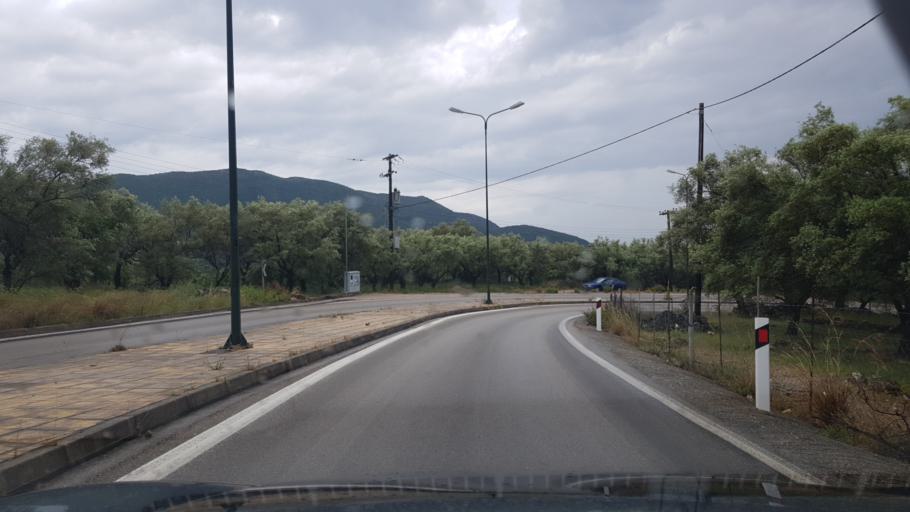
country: GR
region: Ionian Islands
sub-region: Lefkada
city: Nidri
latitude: 38.6500
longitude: 20.6805
